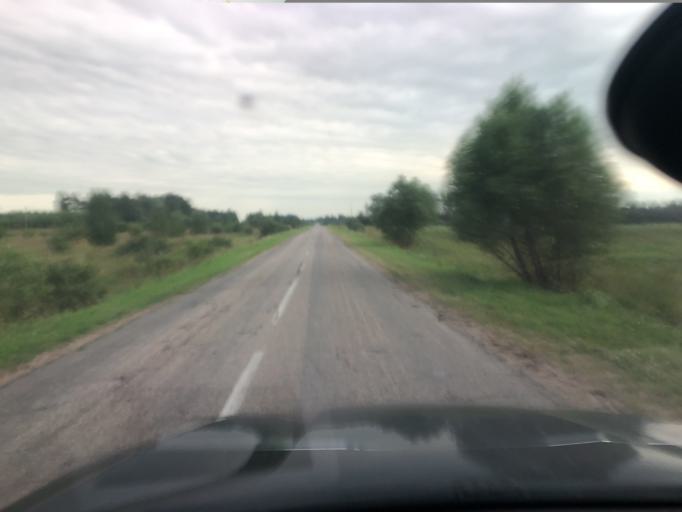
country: RU
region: Jaroslavl
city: Petrovsk
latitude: 57.0029
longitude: 39.0260
